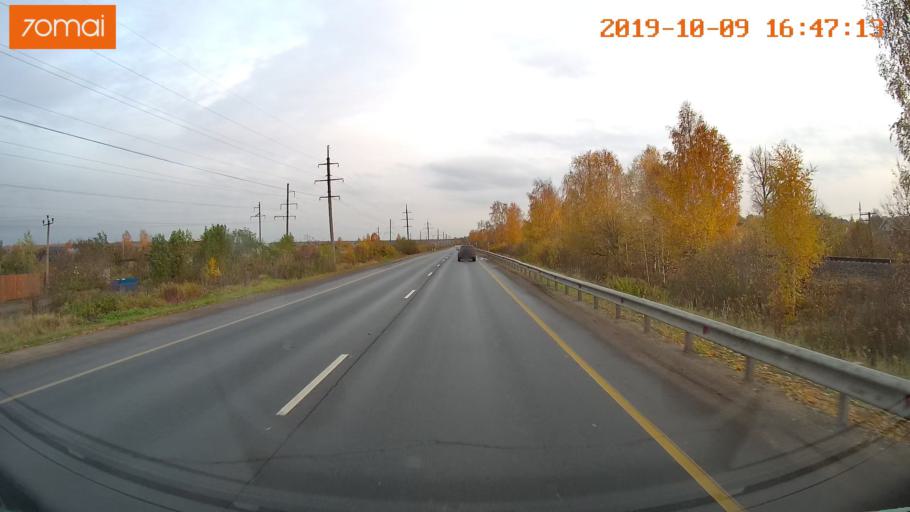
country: RU
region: Kostroma
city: Volgorechensk
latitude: 57.4384
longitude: 41.1748
